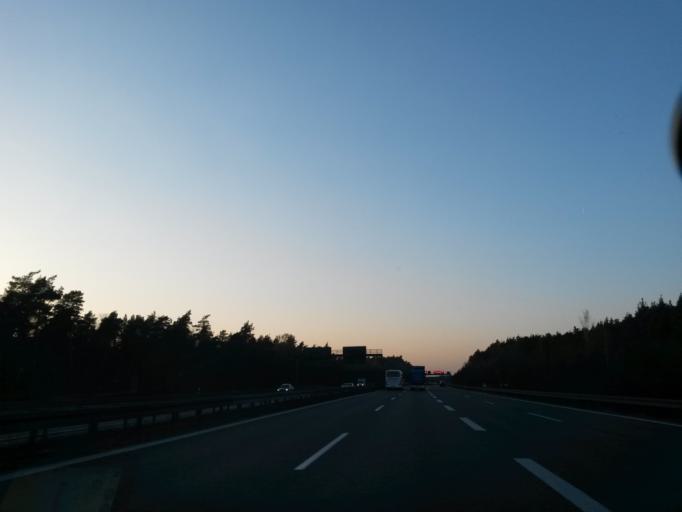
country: DE
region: Bavaria
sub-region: Regierungsbezirk Mittelfranken
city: Wendelstein
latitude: 49.3847
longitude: 11.1262
